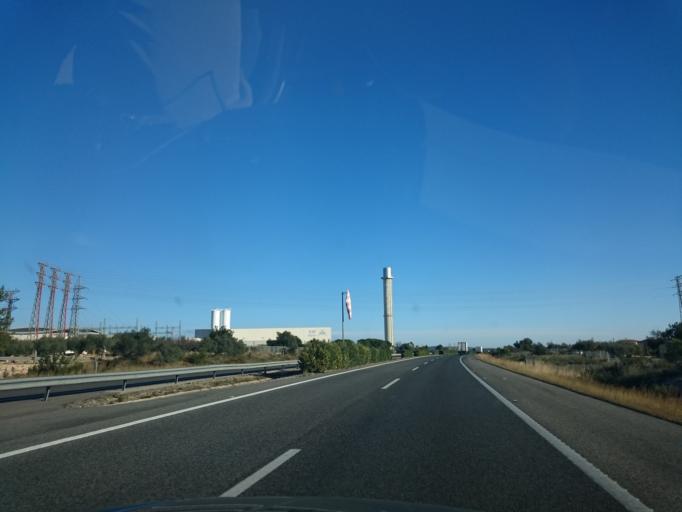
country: ES
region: Catalonia
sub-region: Provincia de Tarragona
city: Camarles
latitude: 40.7984
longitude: 0.6710
